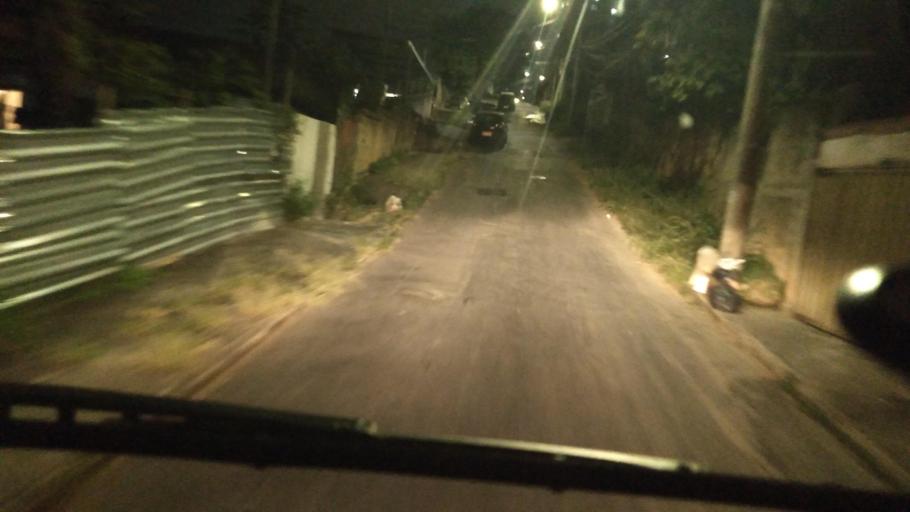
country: BR
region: Minas Gerais
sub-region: Belo Horizonte
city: Belo Horizonte
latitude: -19.9012
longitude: -43.9554
